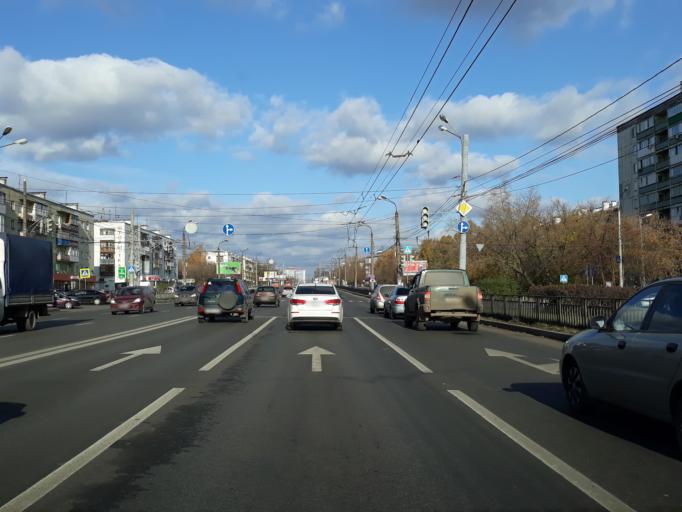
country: RU
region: Nizjnij Novgorod
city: Nizhniy Novgorod
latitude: 56.2871
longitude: 43.9295
